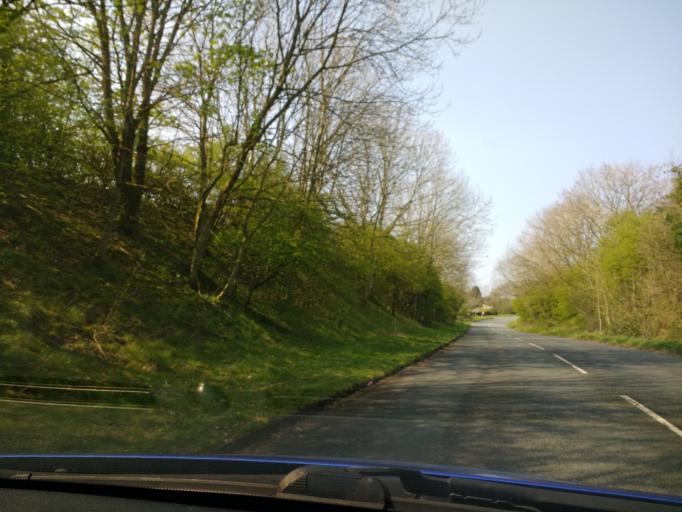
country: GB
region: England
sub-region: Lancashire
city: Bolton le Sands
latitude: 54.0818
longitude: -2.7811
